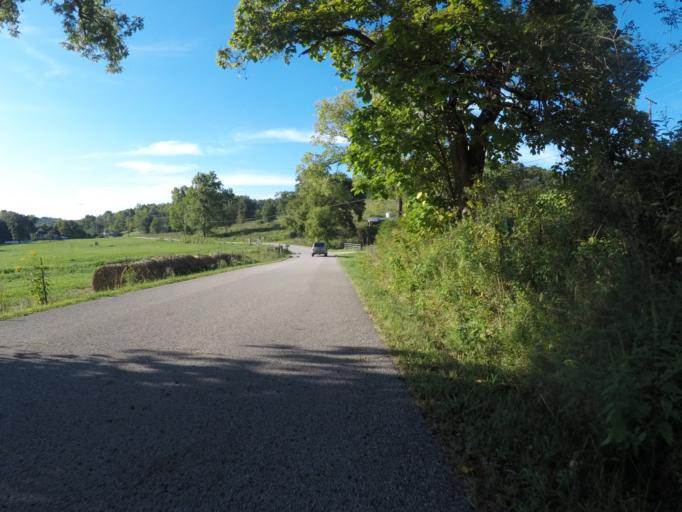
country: US
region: West Virginia
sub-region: Cabell County
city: Huntington
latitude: 38.5060
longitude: -82.4904
